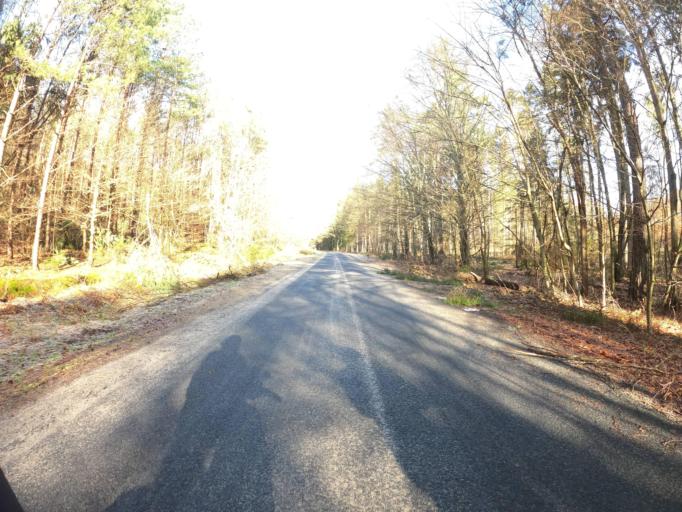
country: PL
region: West Pomeranian Voivodeship
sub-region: Powiat koszalinski
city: Polanow
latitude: 54.1206
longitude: 16.7663
